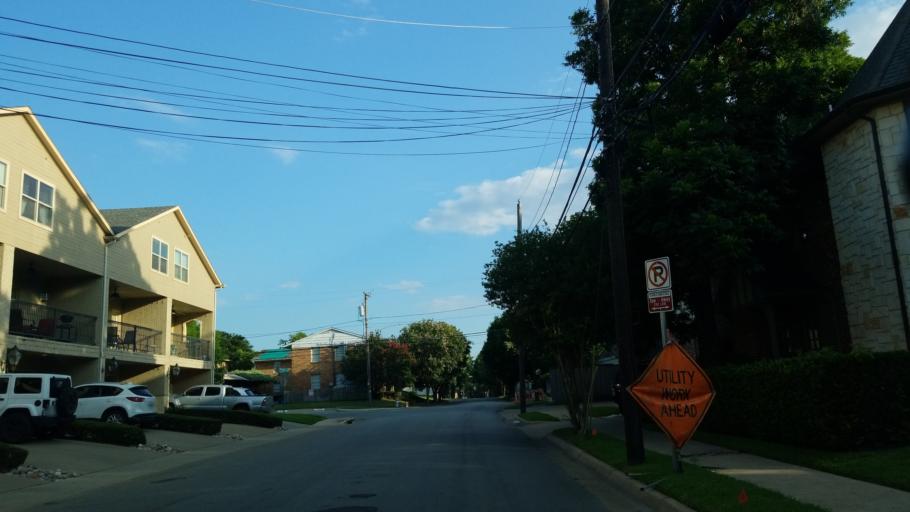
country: US
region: Texas
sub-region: Dallas County
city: University Park
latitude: 32.8472
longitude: -96.7900
